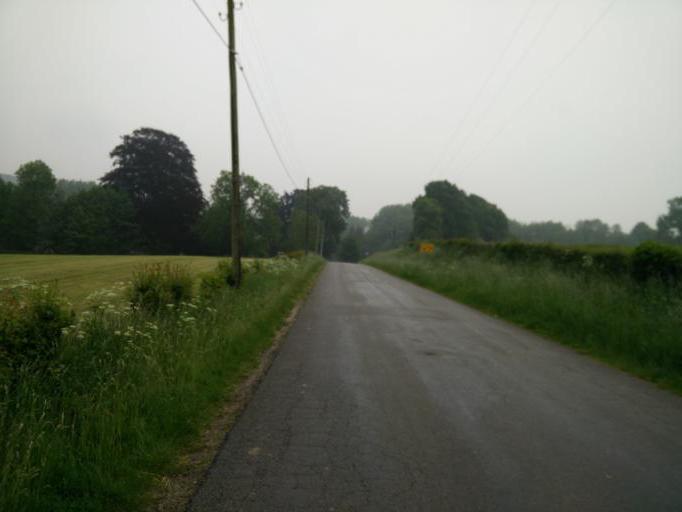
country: BE
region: Wallonia
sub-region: Province de Liege
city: Aubel
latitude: 50.7436
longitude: 5.8873
